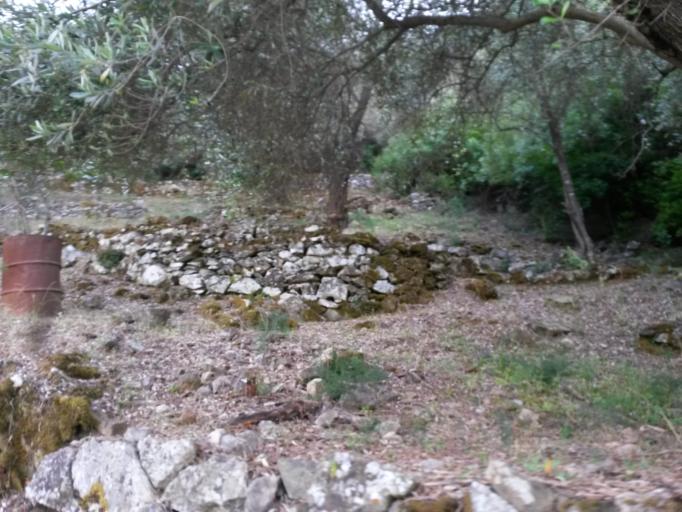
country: GR
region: North Aegean
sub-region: Nomos Lesvou
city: Agiasos
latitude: 39.1109
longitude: 26.3925
